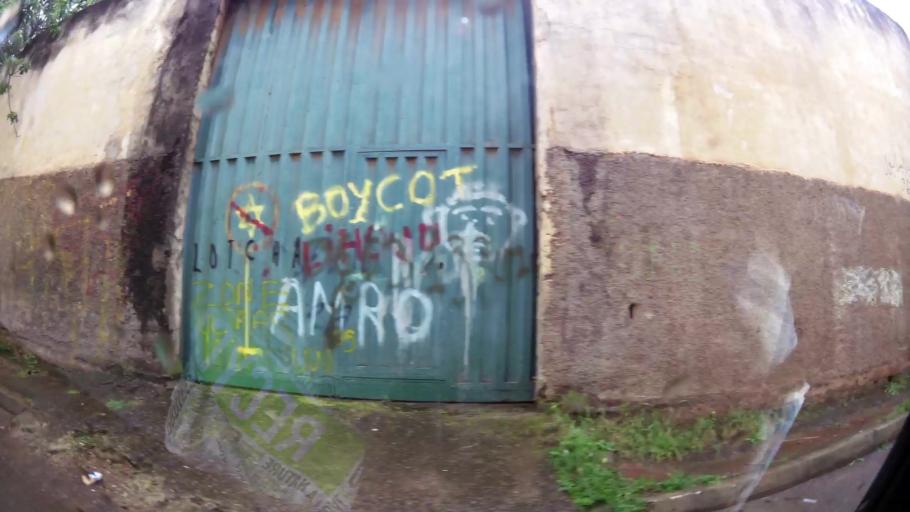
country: MA
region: Grand Casablanca
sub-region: Casablanca
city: Casablanca
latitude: 33.5311
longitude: -7.6522
